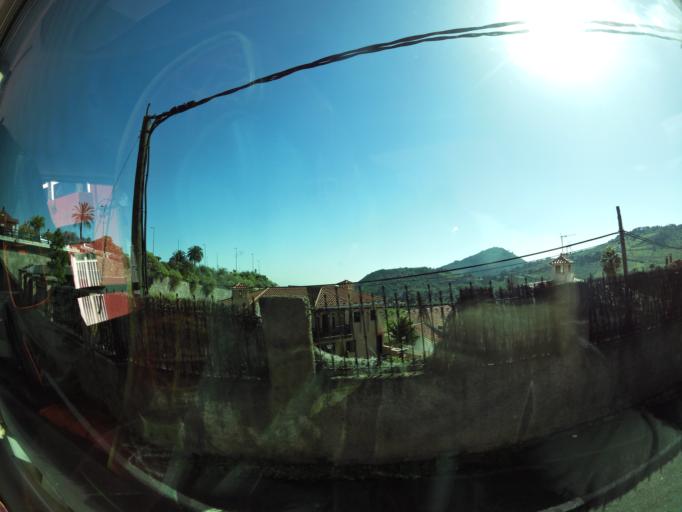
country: ES
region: Canary Islands
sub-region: Provincia de Las Palmas
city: Santa Brigida
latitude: 28.0455
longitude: -15.4747
